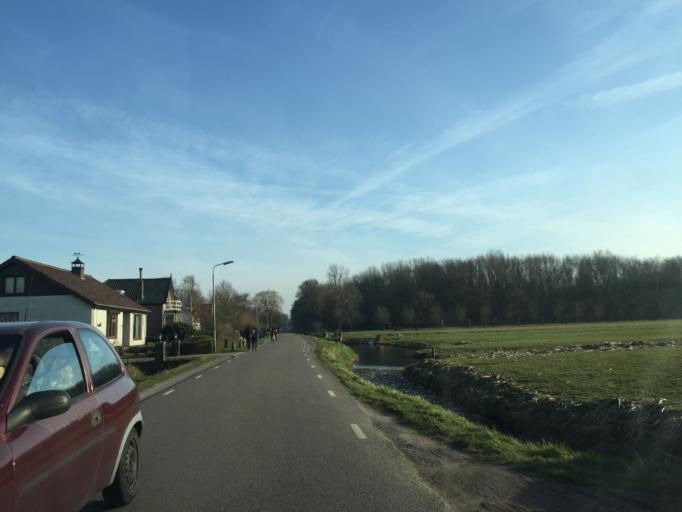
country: NL
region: South Holland
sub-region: Gemeente Den Haag
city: Ypenburg
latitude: 52.0184
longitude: 4.3898
